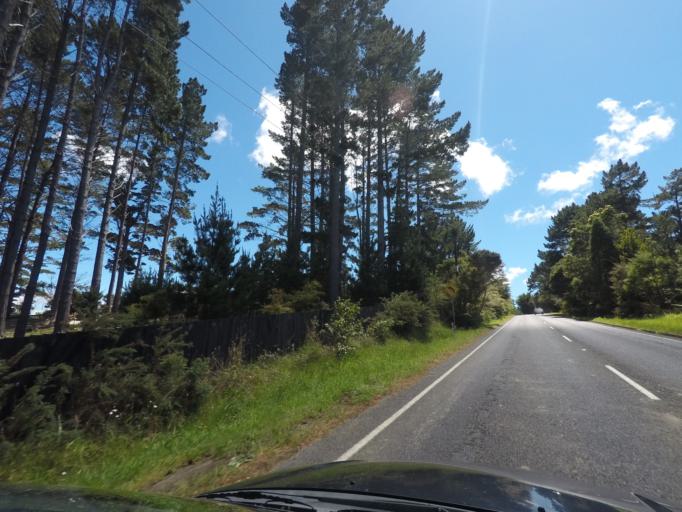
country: NZ
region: Auckland
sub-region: Auckland
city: Rothesay Bay
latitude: -36.7413
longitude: 174.6747
